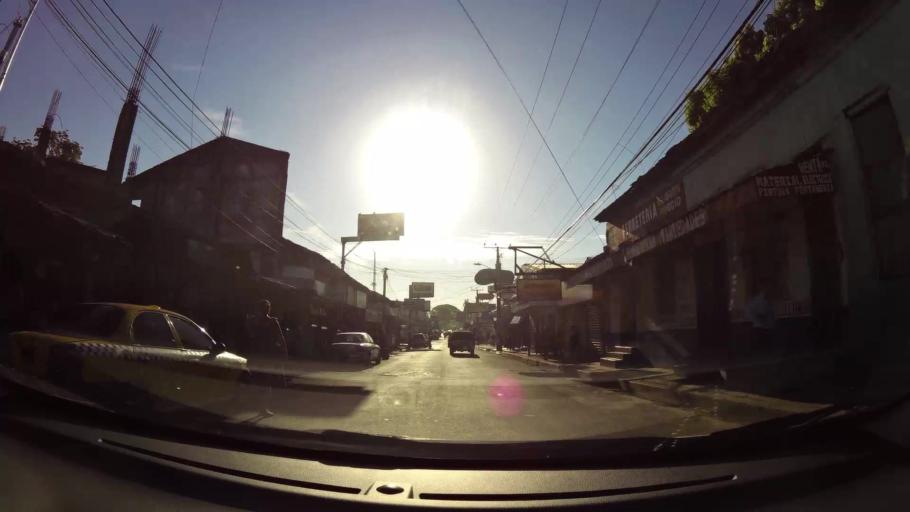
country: SV
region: Sonsonate
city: Sonsonate
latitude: 13.7182
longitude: -89.7245
